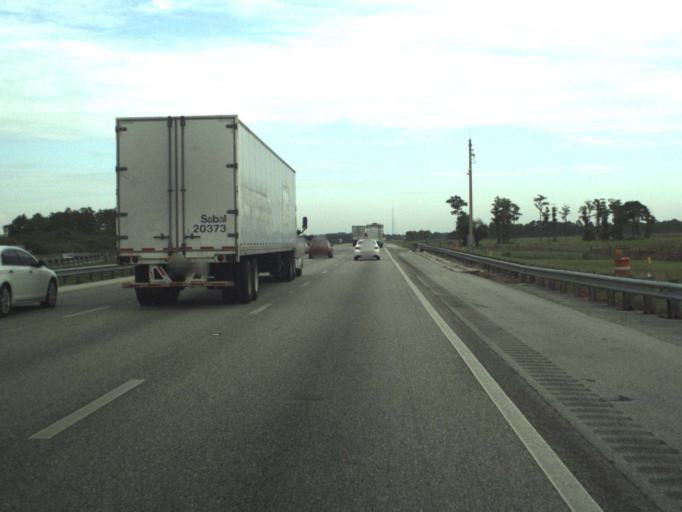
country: US
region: Florida
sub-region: Martin County
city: Port Salerno
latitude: 27.0581
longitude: -80.2379
